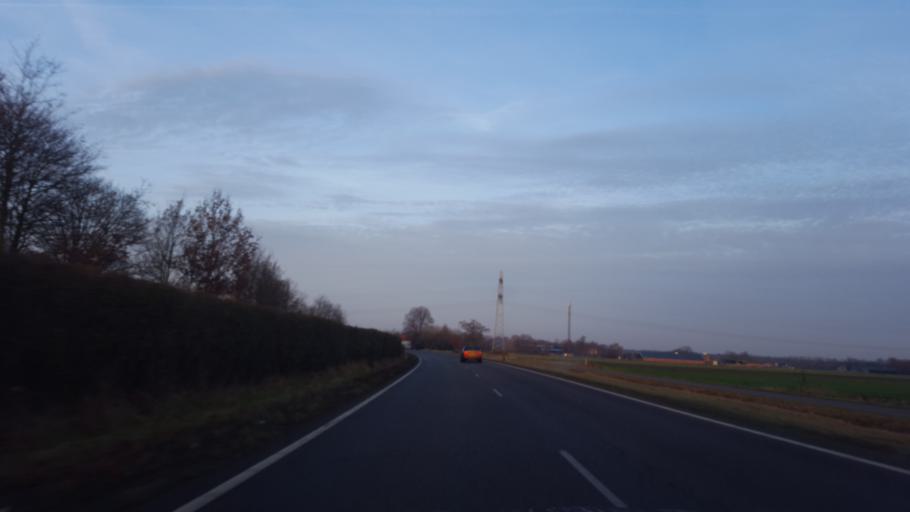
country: NL
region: Limburg
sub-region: Gemeente Weert
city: Weert
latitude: 51.2672
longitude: 5.6852
